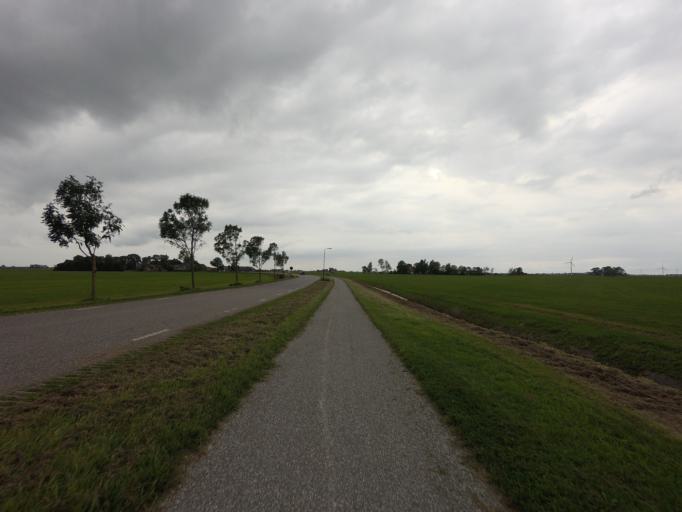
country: NL
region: Friesland
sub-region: Sudwest Fryslan
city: Bolsward
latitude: 53.0406
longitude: 5.5476
